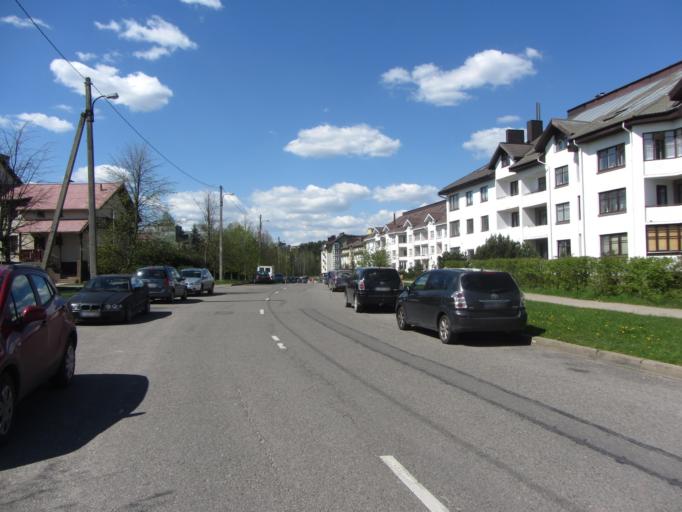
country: LT
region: Vilnius County
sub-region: Vilnius
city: Fabijoniskes
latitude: 54.7502
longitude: 25.2733
